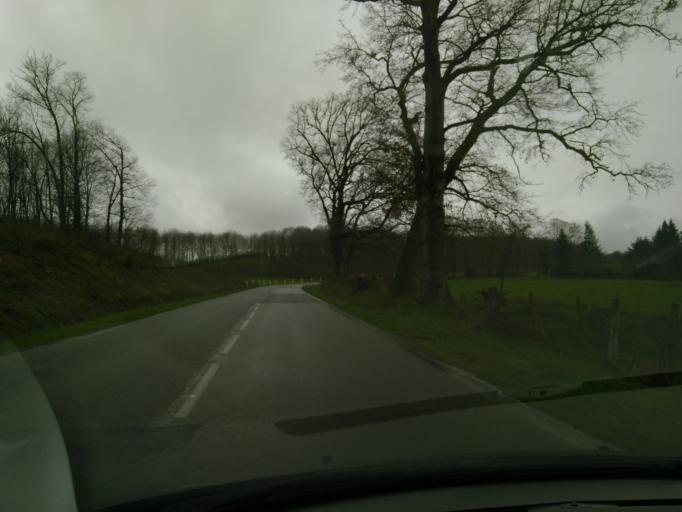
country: FR
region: Limousin
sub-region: Departement de la Haute-Vienne
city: Solignac
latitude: 45.7310
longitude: 1.2676
